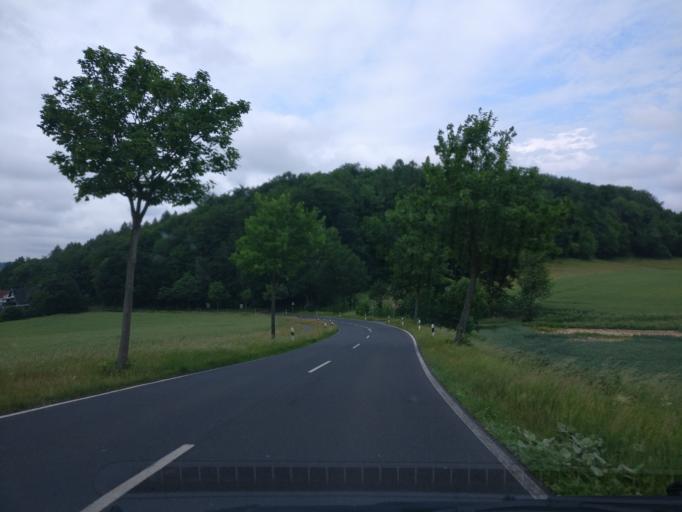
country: DE
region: Lower Saxony
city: Hannoversch Munden
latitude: 51.4190
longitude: 9.6922
